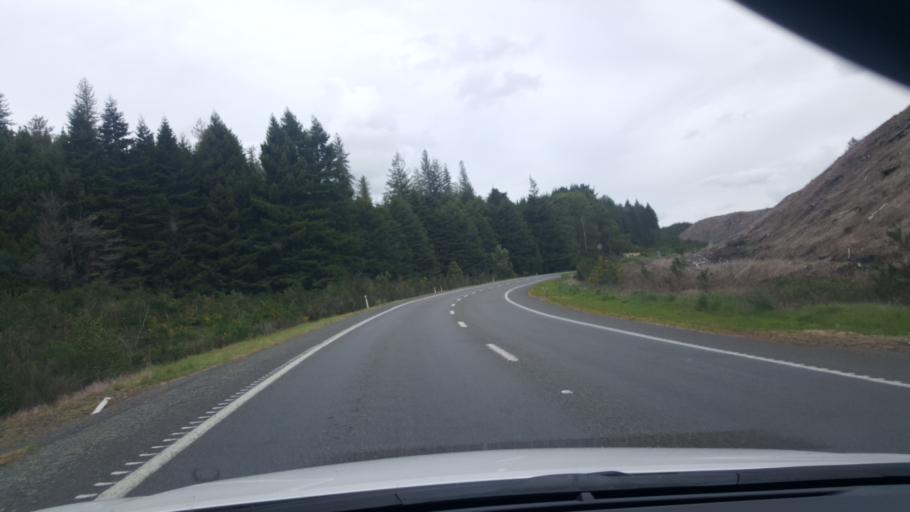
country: NZ
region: Bay of Plenty
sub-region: Rotorua District
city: Rotorua
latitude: -38.2283
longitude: 176.2966
